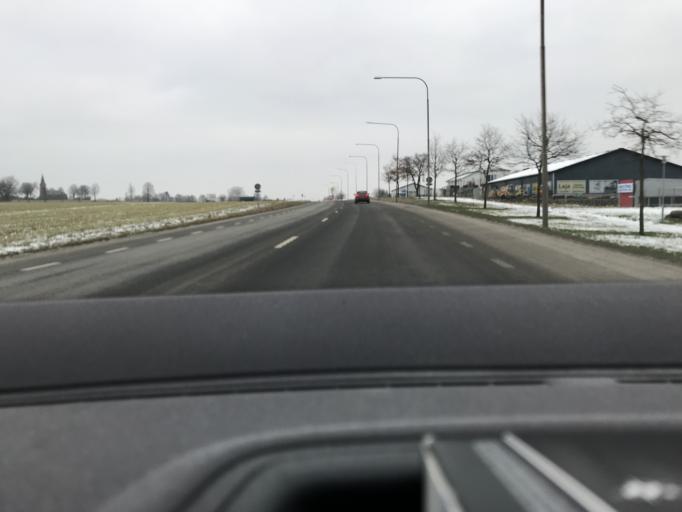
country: SE
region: Skane
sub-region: Ystads Kommun
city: Ystad
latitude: 55.4464
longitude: 13.8405
